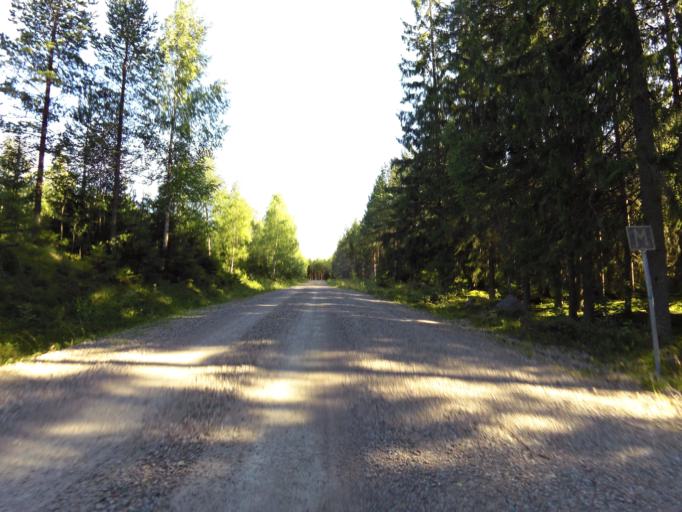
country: SE
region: Gaevleborg
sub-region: Hofors Kommun
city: Hofors
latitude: 60.6483
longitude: 16.2688
